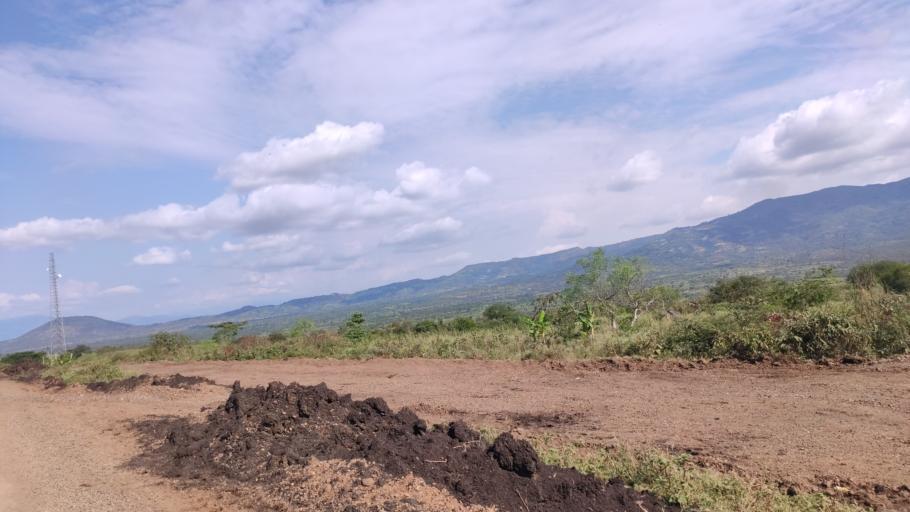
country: ET
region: Southern Nations, Nationalities, and People's Region
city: Felege Neway
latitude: 6.3962
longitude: 37.1080
